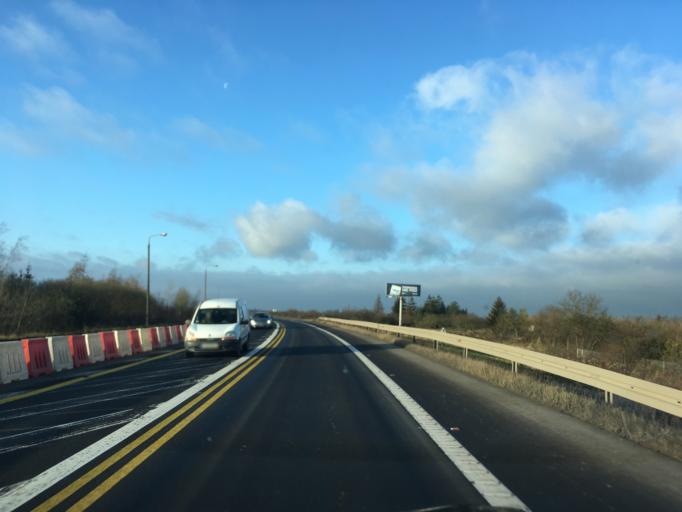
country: PL
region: Kujawsko-Pomorskie
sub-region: Powiat swiecki
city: Swiecie
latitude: 53.4204
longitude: 18.4653
